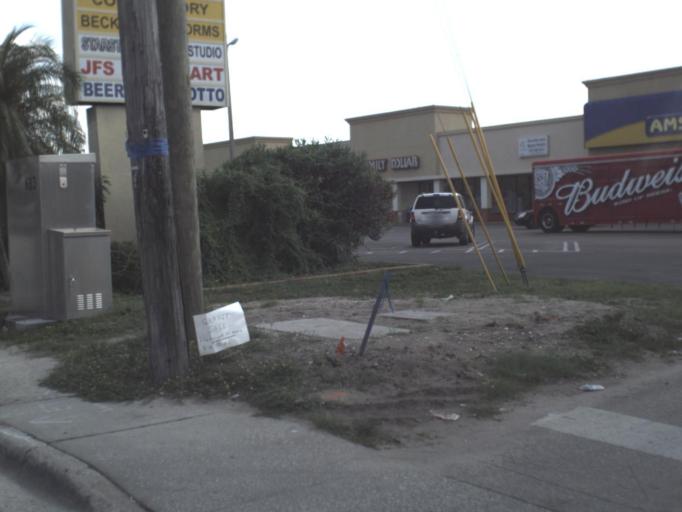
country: US
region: Florida
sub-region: Pinellas County
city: Ridgecrest
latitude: 27.8801
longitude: -82.7870
